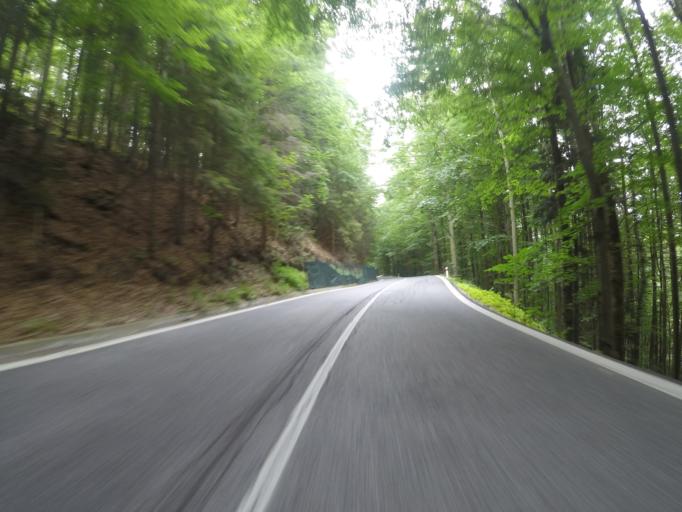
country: SK
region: Kosicky
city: Dobsina
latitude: 48.8528
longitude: 20.4611
